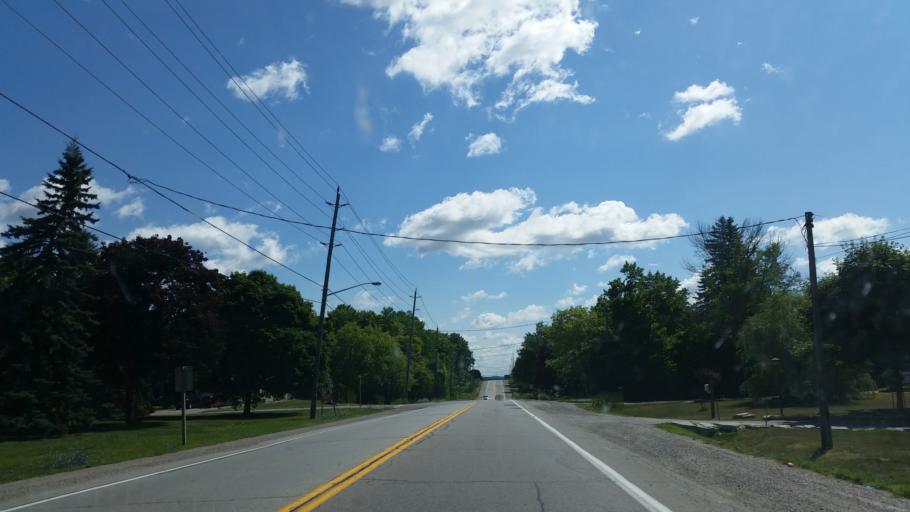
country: CA
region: Ontario
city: Vaughan
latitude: 43.8984
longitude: -79.6705
